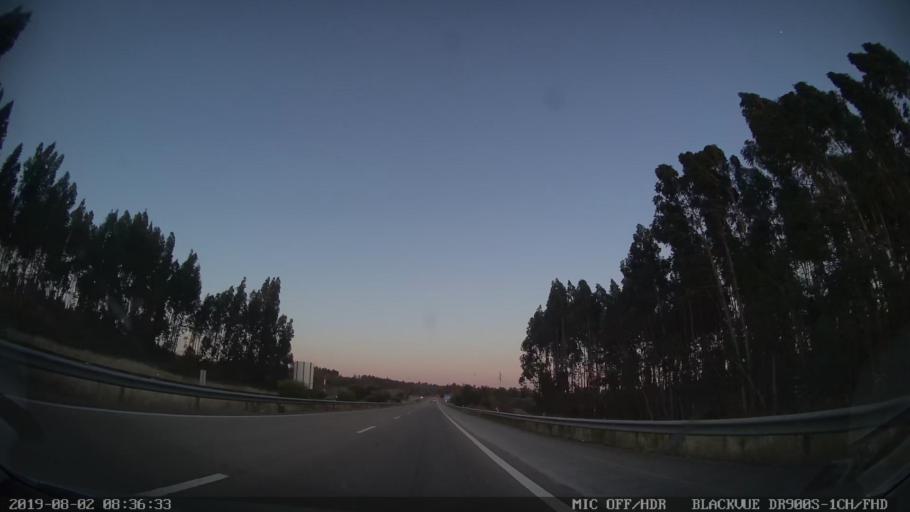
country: PT
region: Santarem
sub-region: Constancia
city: Constancia
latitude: 39.4866
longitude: -8.3798
